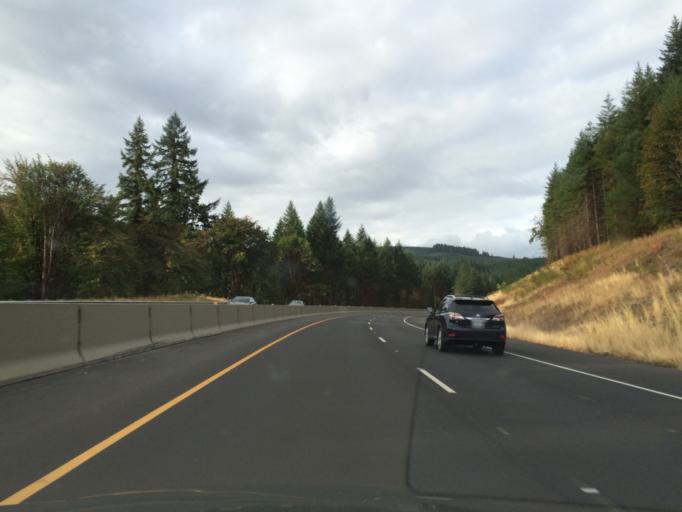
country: US
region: Oregon
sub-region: Lane County
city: Cottage Grove
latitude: 43.7446
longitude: -123.1814
